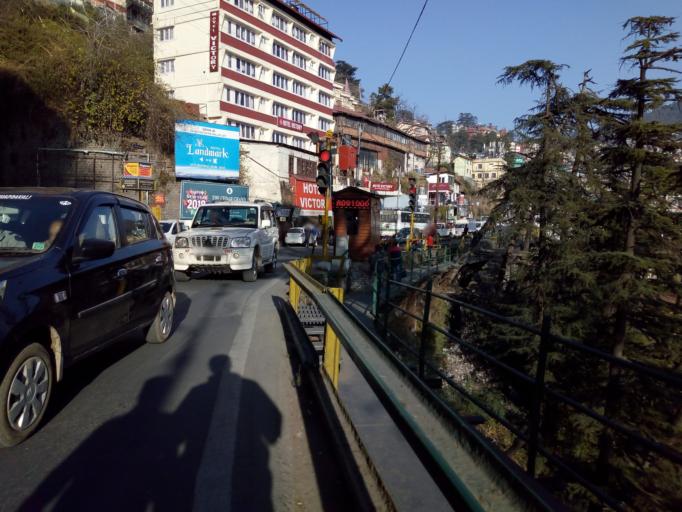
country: IN
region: Himachal Pradesh
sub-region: Shimla
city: Shimla
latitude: 31.1047
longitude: 77.1637
